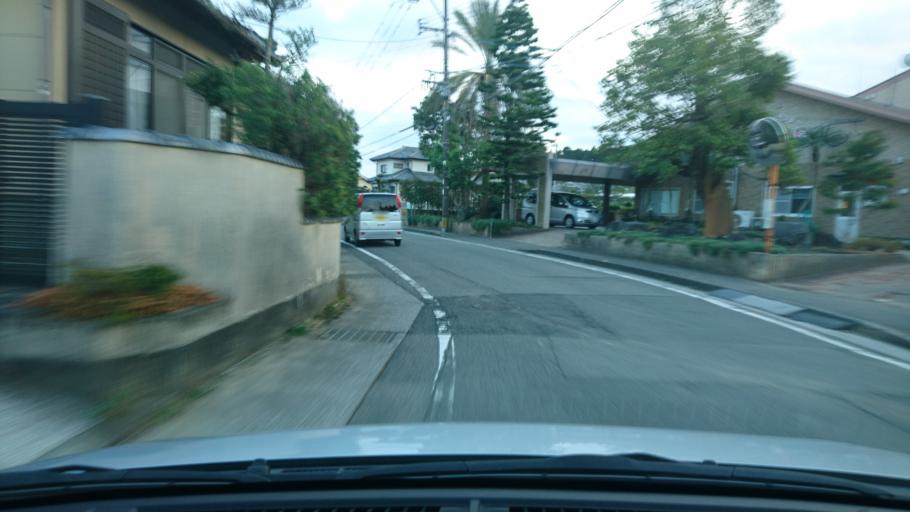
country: JP
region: Miyazaki
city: Miyazaki-shi
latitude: 31.8658
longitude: 131.4267
